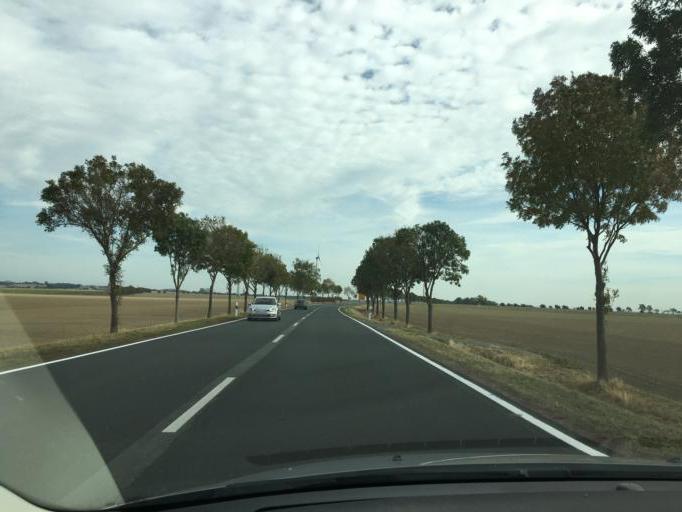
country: DE
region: Saxony
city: Stauchitz
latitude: 51.2792
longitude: 13.1863
